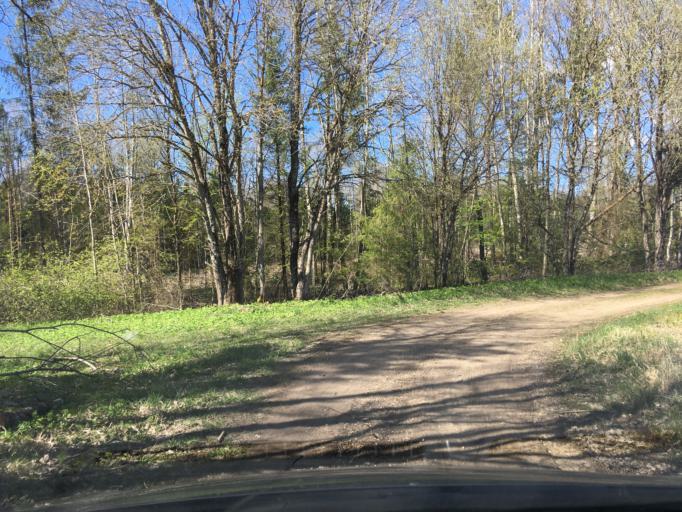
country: EE
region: Harju
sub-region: Raasiku vald
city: Arukula
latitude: 59.2054
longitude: 25.1215
